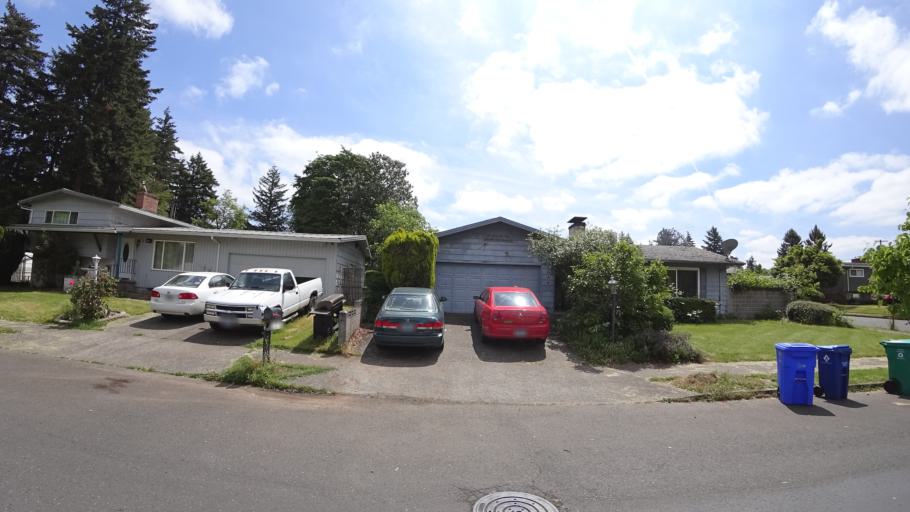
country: US
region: Oregon
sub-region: Multnomah County
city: Gresham
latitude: 45.5005
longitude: -122.4898
